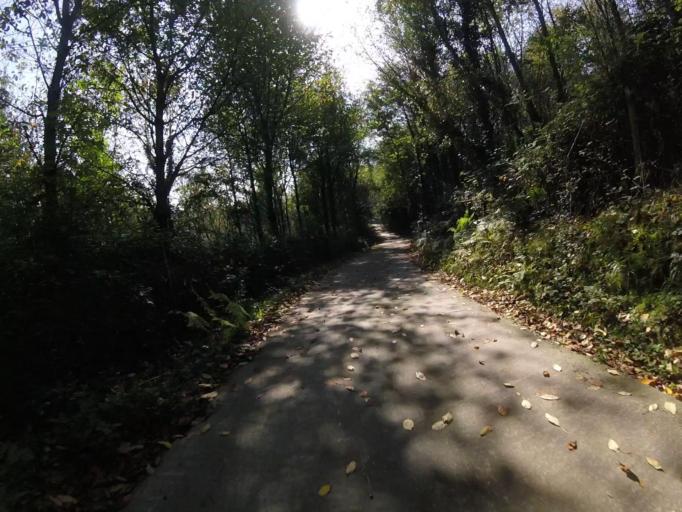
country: ES
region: Basque Country
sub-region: Provincia de Guipuzcoa
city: Irun
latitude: 43.3267
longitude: -1.7563
